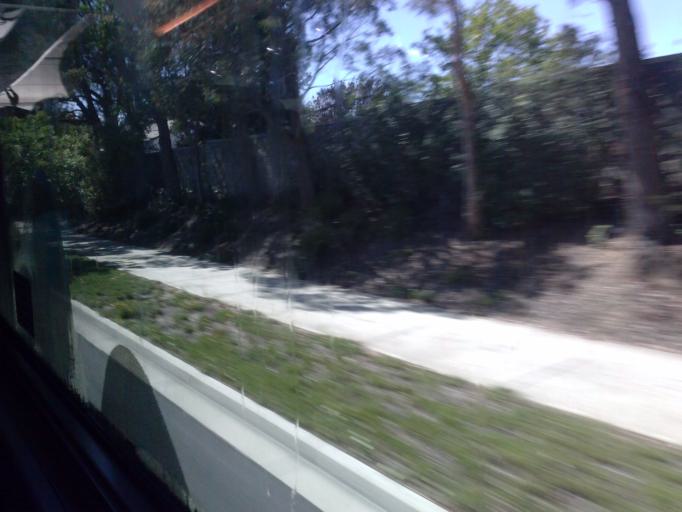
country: US
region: California
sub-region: Alameda County
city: Livermore
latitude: 37.6611
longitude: -121.7641
